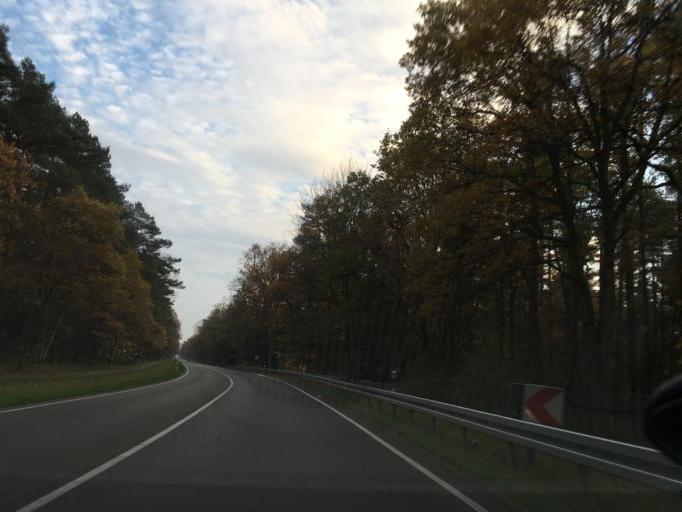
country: DE
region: Lower Saxony
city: Winsen
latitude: 52.7212
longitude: 9.9708
